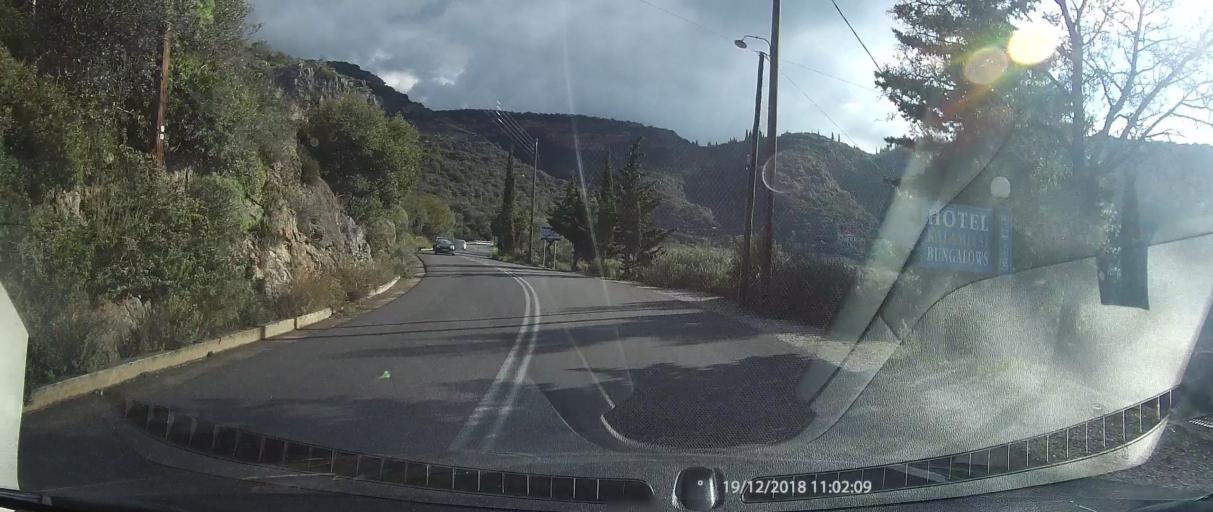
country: GR
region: Peloponnese
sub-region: Nomos Messinias
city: Kardamyli
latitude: 36.8815
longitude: 22.2396
